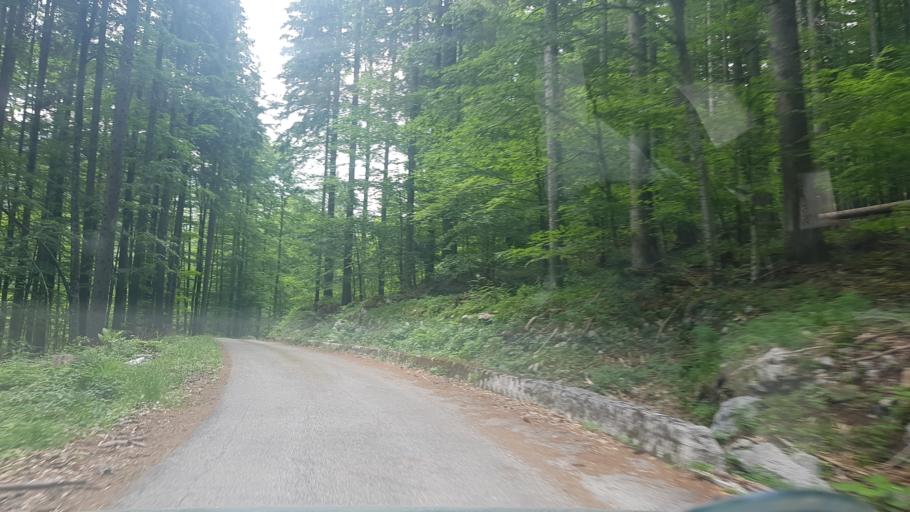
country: IT
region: Friuli Venezia Giulia
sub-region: Provincia di Udine
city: Paularo
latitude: 46.5354
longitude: 13.2084
